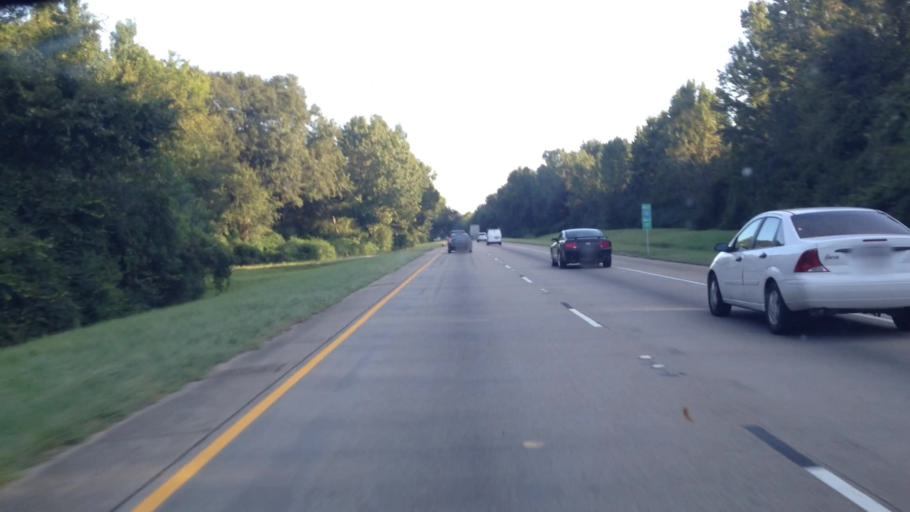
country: US
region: Louisiana
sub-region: Ascension Parish
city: Prairieville
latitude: 30.2988
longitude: -90.9919
